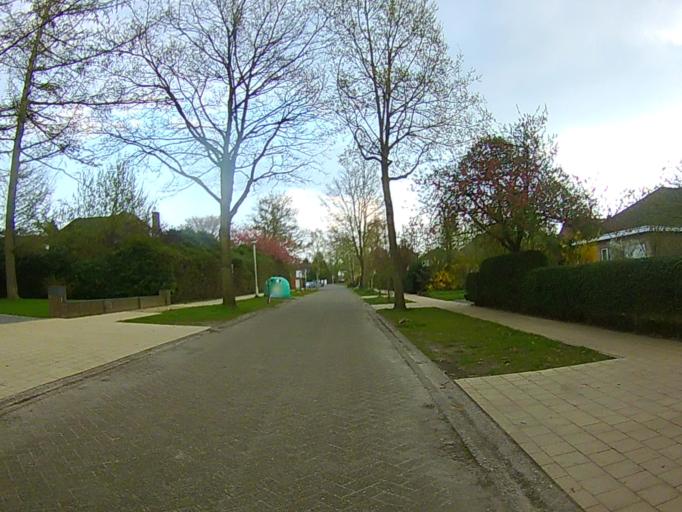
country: BE
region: Flanders
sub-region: Provincie Antwerpen
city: Kapellen
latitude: 51.3019
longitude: 4.4408
